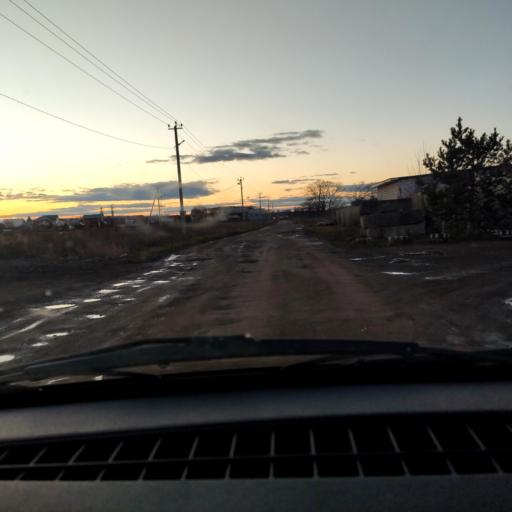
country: RU
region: Bashkortostan
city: Ufa
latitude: 54.6446
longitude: 55.9139
